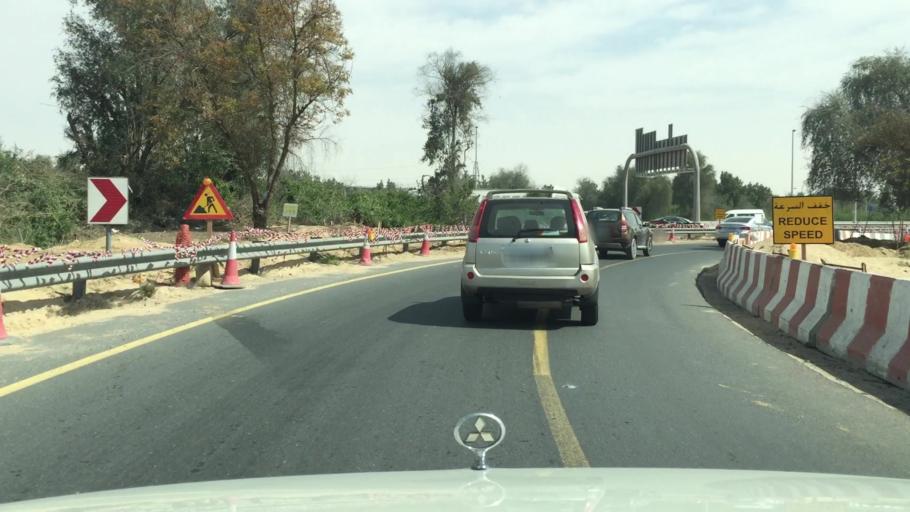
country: AE
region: Dubai
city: Dubai
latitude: 25.0991
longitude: 55.3815
